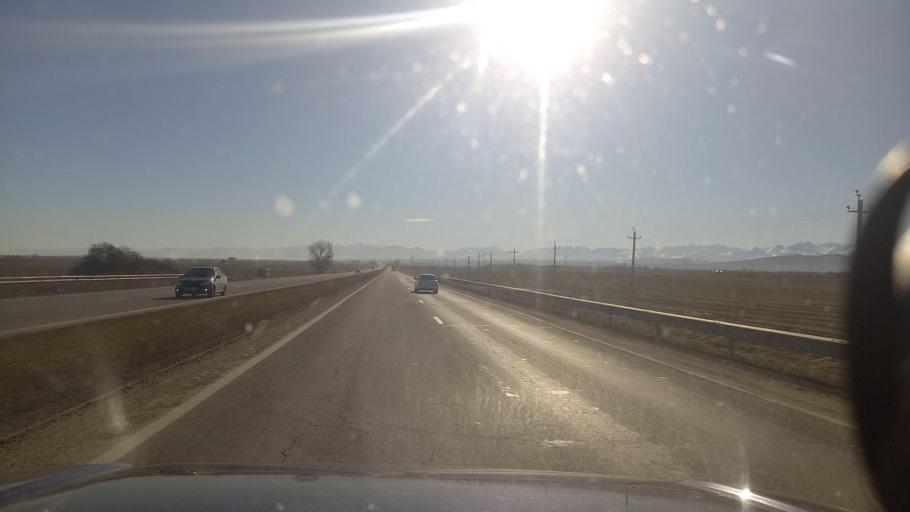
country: RU
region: Kabardino-Balkariya
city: Germenchik
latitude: 43.5586
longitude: 43.7254
